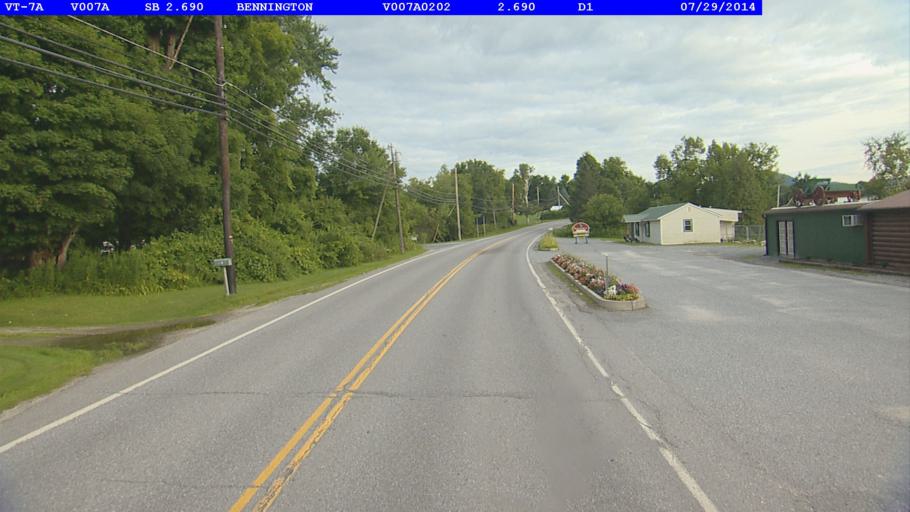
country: US
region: Vermont
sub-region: Bennington County
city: North Bennington
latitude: 42.9282
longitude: -73.2086
